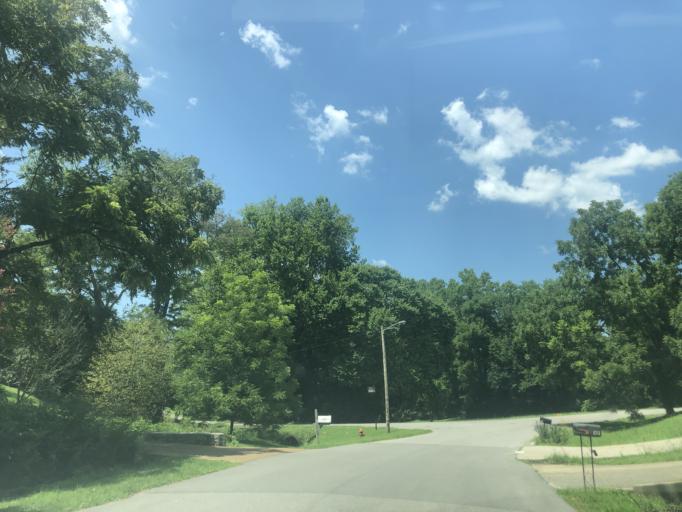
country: US
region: Tennessee
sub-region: Davidson County
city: Nashville
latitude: 36.1725
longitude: -86.6951
